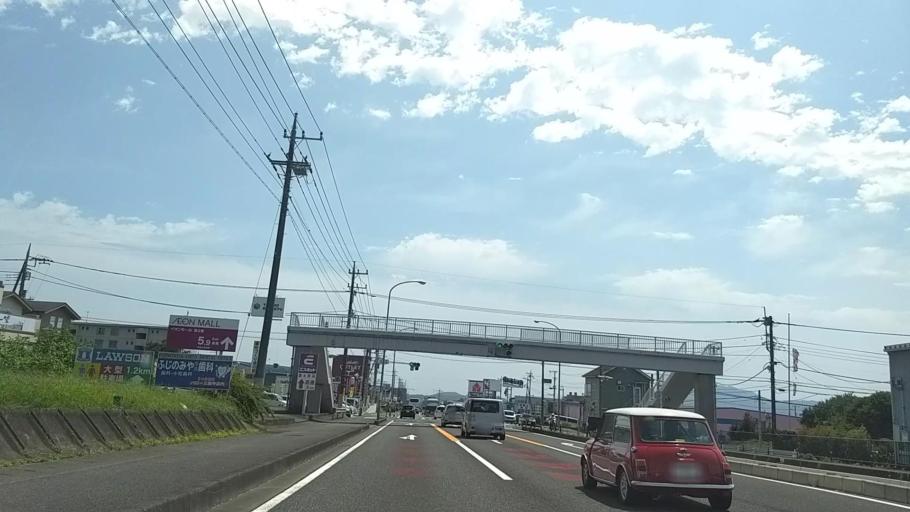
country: JP
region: Shizuoka
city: Fujinomiya
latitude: 35.2508
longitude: 138.6168
